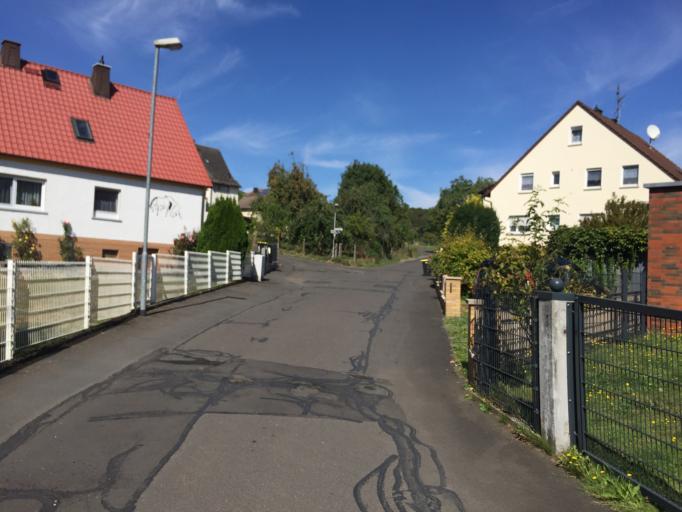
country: DE
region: Hesse
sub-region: Regierungsbezirk Giessen
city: Reiskirchen
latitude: 50.5975
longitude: 8.8828
